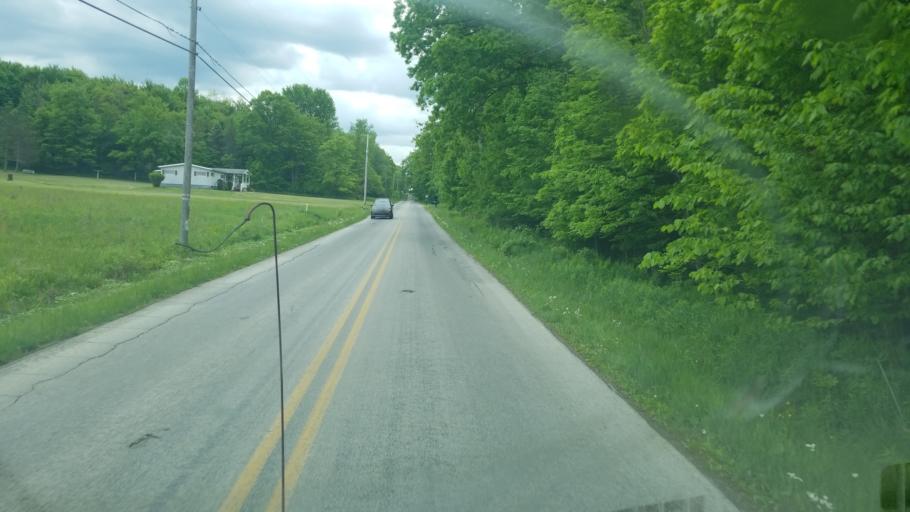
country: US
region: Pennsylvania
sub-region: Venango County
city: Franklin
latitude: 41.2131
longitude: -79.8451
